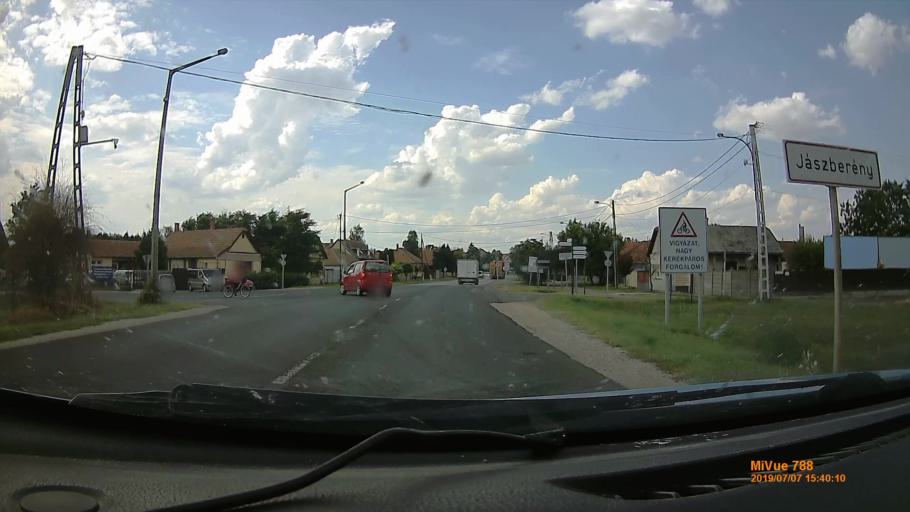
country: HU
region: Jasz-Nagykun-Szolnok
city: Jaszbereny
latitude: 47.4959
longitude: 19.9291
